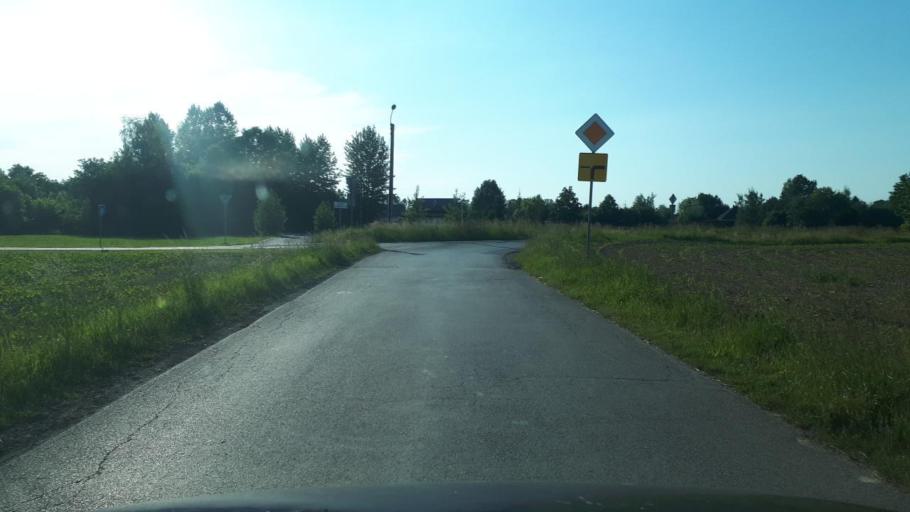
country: PL
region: Silesian Voivodeship
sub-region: Powiat bielski
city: Bronow
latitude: 49.8719
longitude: 18.9266
